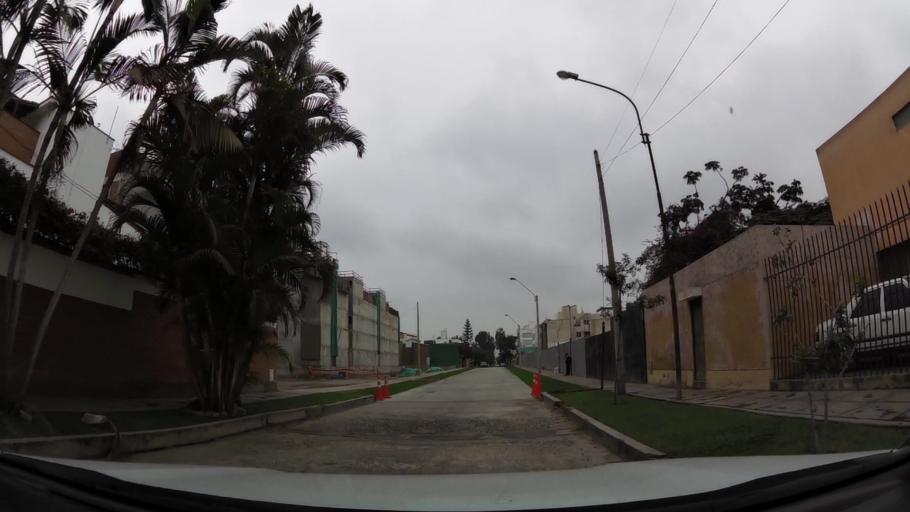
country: PE
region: Lima
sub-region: Lima
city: Surco
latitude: -12.1289
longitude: -77.0054
